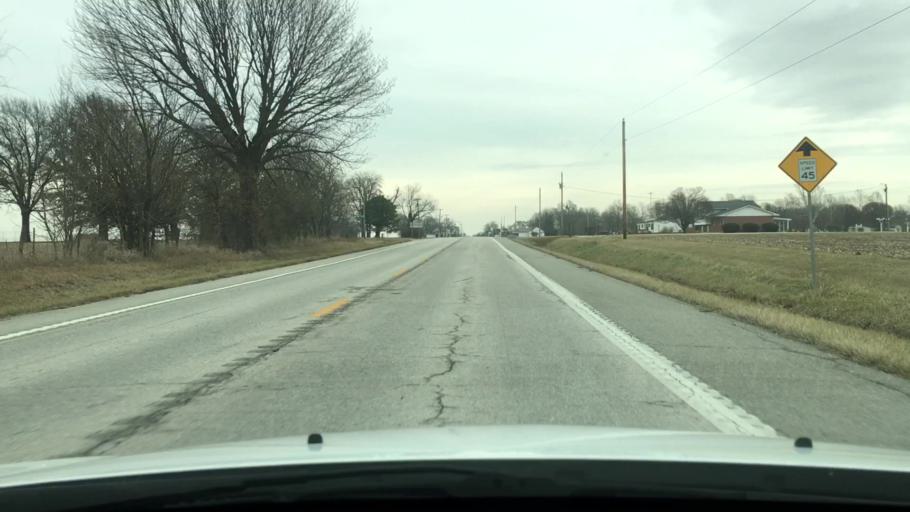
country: US
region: Missouri
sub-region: Audrain County
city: Vandalia
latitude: 39.2794
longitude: -91.5824
